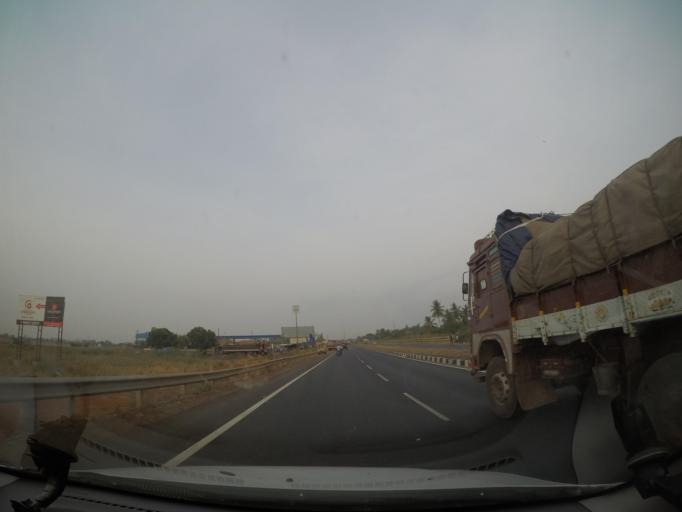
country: IN
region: Andhra Pradesh
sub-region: Krishna
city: Gannavaram
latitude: 16.6051
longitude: 80.9024
